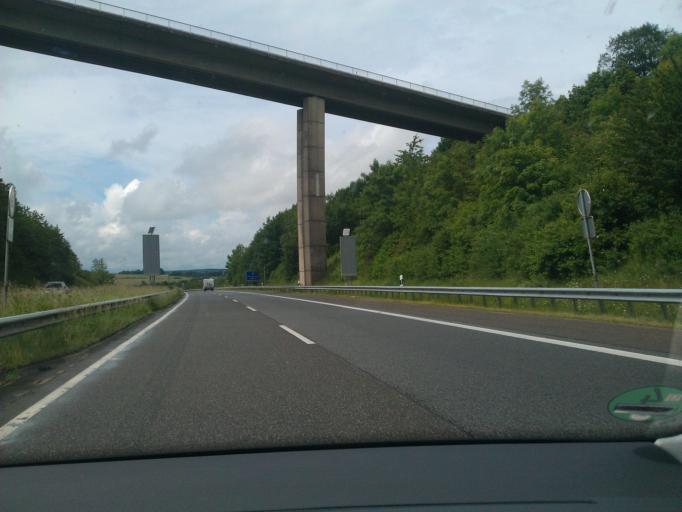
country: DE
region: Rheinland-Pfalz
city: Heisdorf
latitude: 50.1173
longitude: 6.4358
